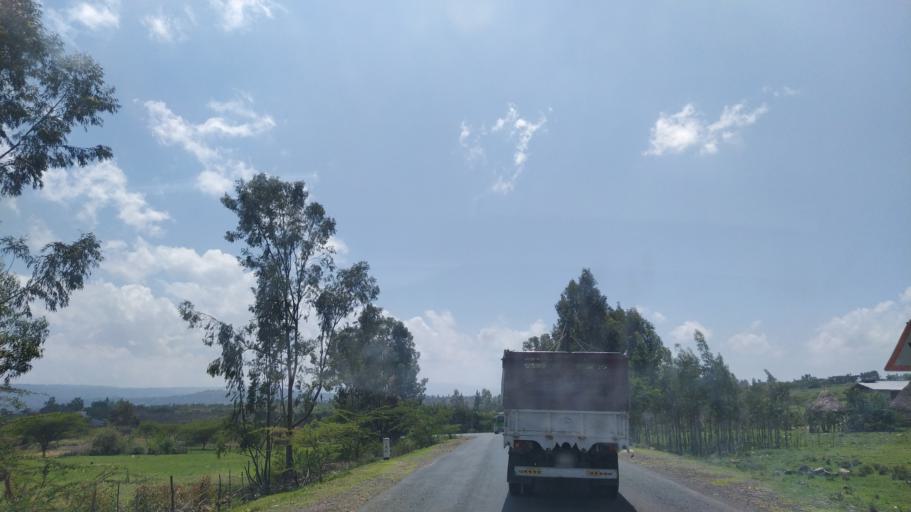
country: ET
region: Southern Nations, Nationalities, and People's Region
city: Butajira
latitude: 7.7715
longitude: 38.1388
